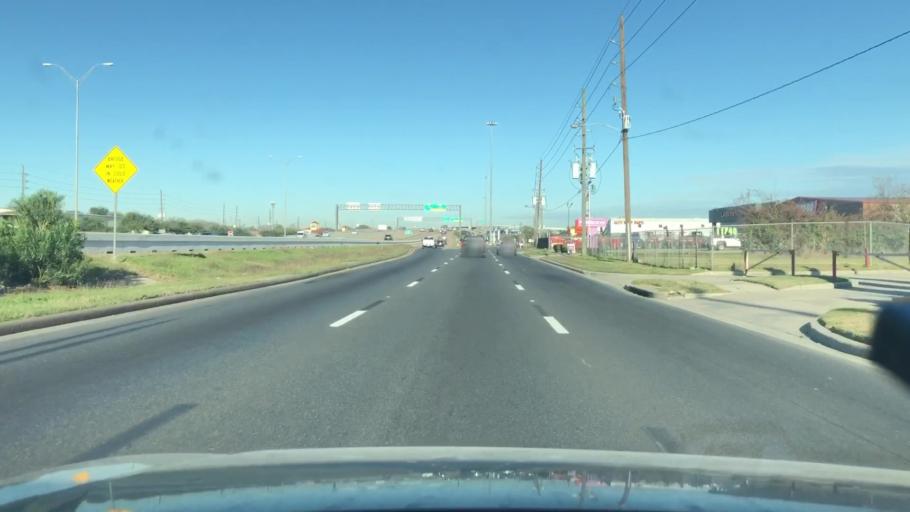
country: US
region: Texas
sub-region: Fort Bend County
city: Missouri City
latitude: 29.6509
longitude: -95.5465
